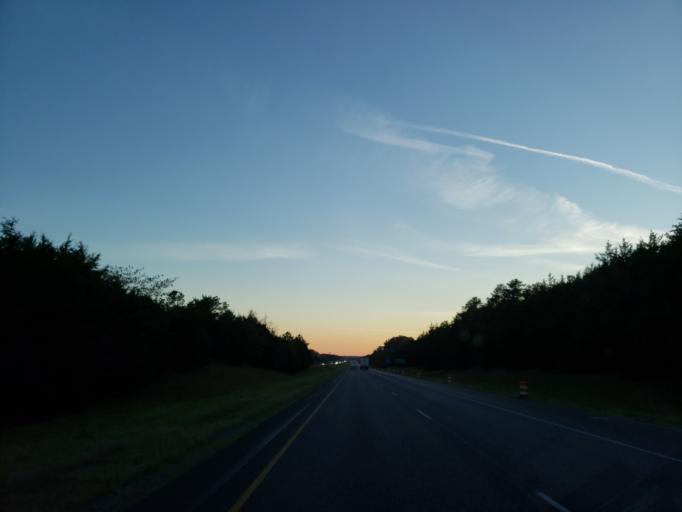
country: US
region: Alabama
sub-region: Sumter County
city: Livingston
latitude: 32.6424
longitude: -88.1987
